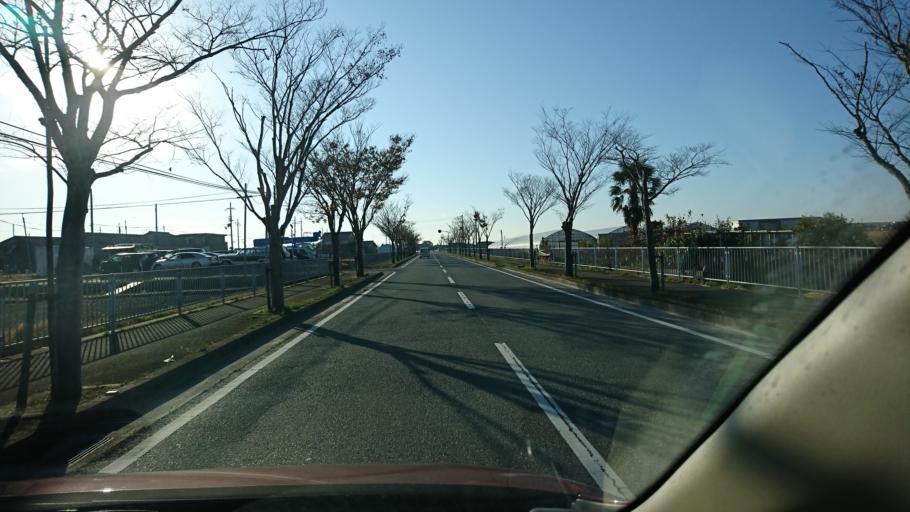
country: JP
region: Hyogo
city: Miki
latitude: 34.7696
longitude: 134.9113
